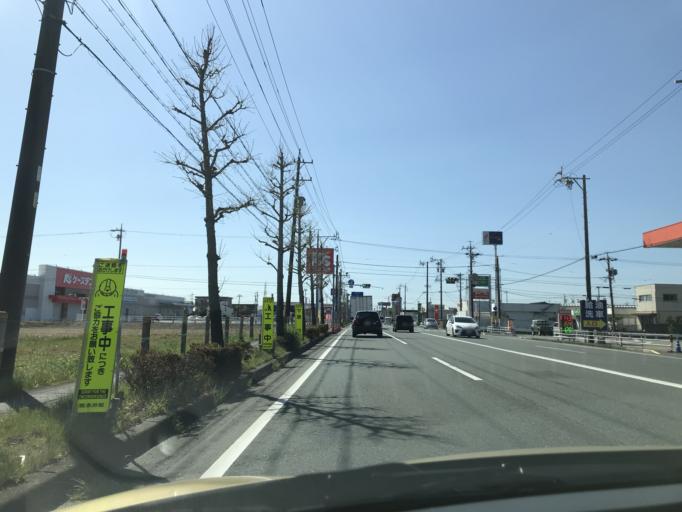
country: JP
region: Shizuoka
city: Fukuroi
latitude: 34.7580
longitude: 137.9058
